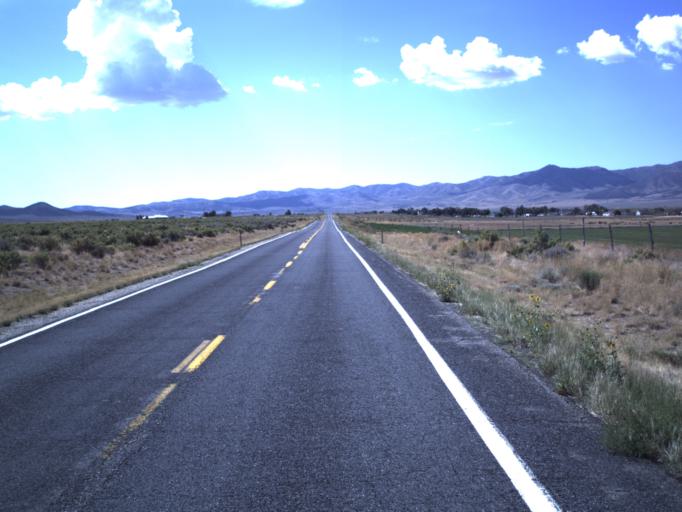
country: US
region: Utah
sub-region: Tooele County
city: Tooele
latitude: 40.1130
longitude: -112.4308
